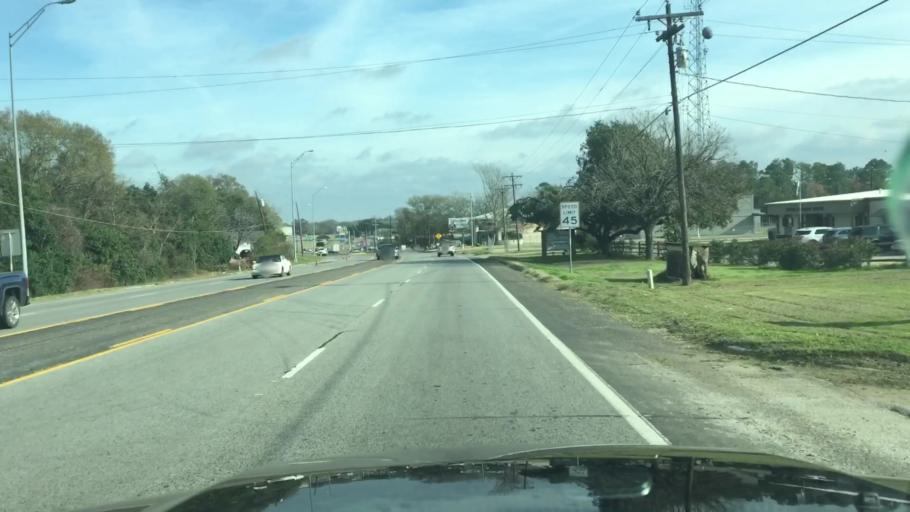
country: US
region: Texas
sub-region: Washington County
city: Brenham
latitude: 30.1671
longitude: -96.4329
